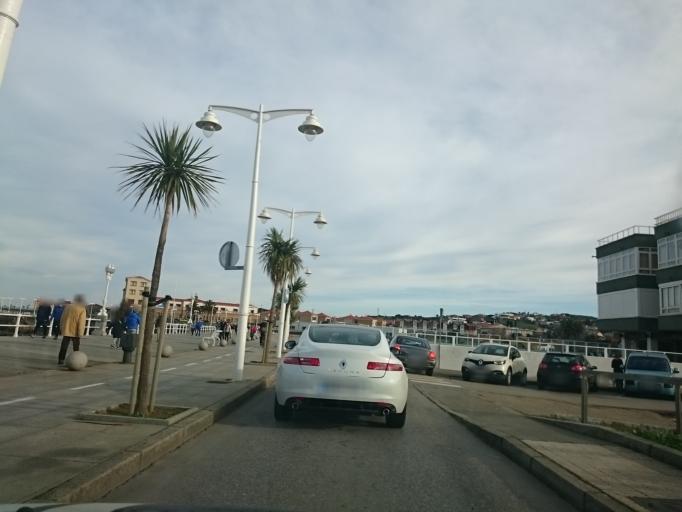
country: ES
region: Asturias
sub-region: Province of Asturias
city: Gijon
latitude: 43.5417
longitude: -5.6074
